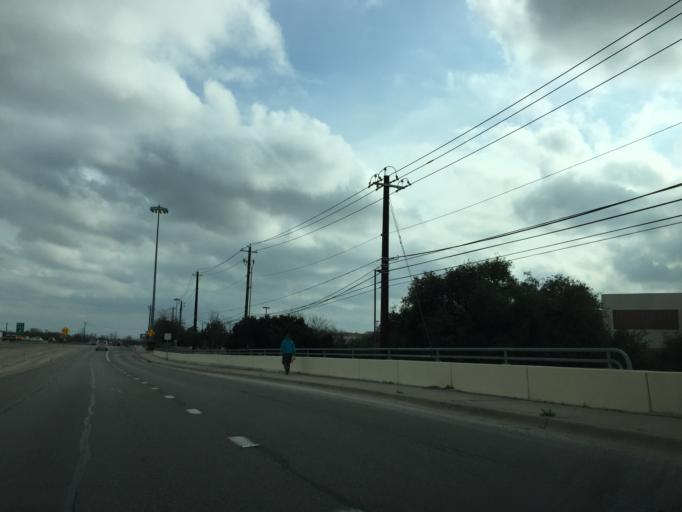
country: US
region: Texas
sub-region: Travis County
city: Wells Branch
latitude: 30.3982
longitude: -97.6734
